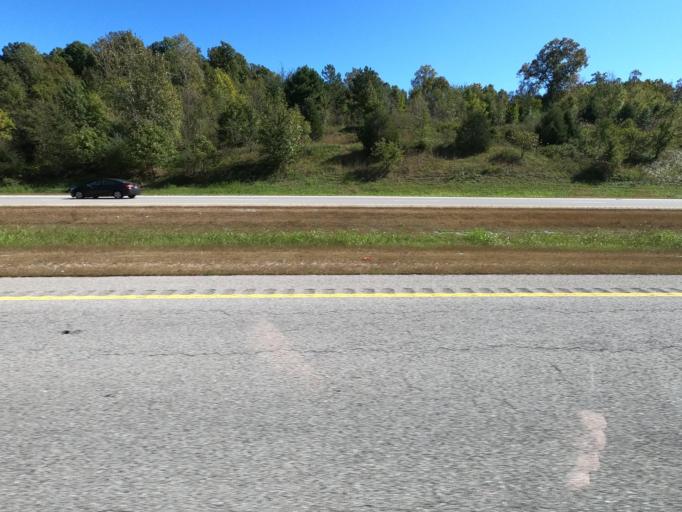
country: US
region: Tennessee
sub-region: Maury County
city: Mount Pleasant
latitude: 35.4679
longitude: -87.2657
